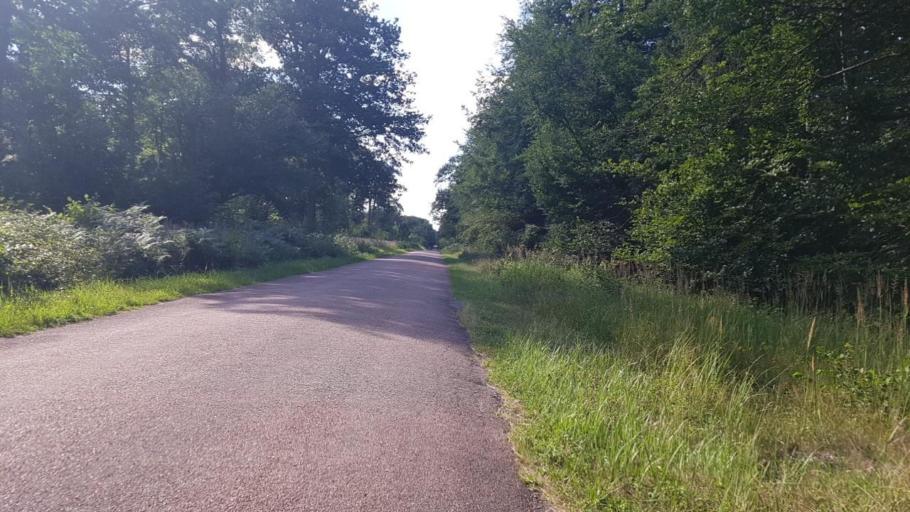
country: FR
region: Picardie
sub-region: Departement de l'Oise
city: Ver-sur-Launette
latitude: 49.1455
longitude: 2.6482
